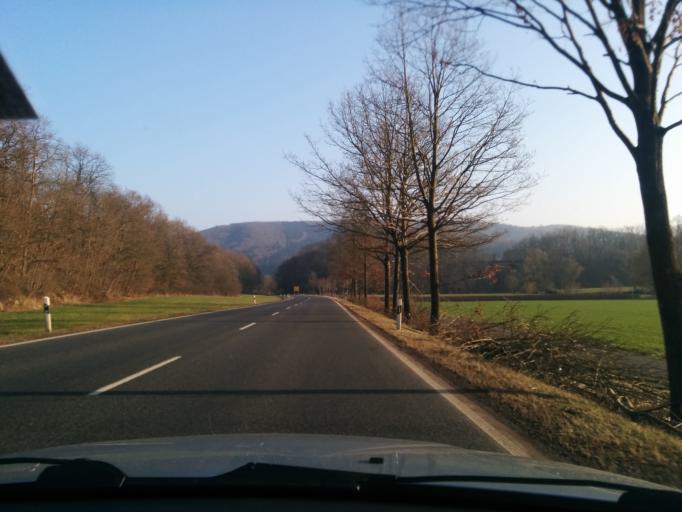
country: DE
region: Hesse
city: Waldkappel
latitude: 51.1511
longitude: 9.8741
